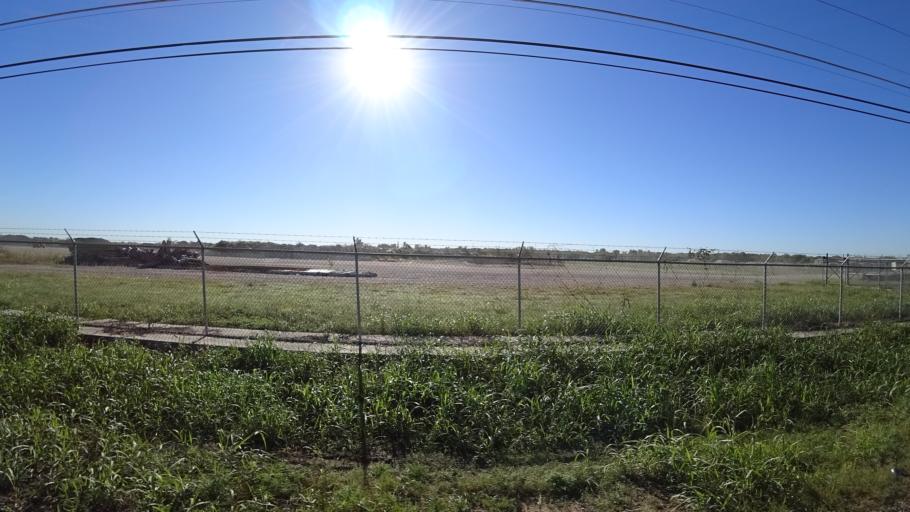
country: US
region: Texas
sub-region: Travis County
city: Austin
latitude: 30.2322
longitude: -97.6685
